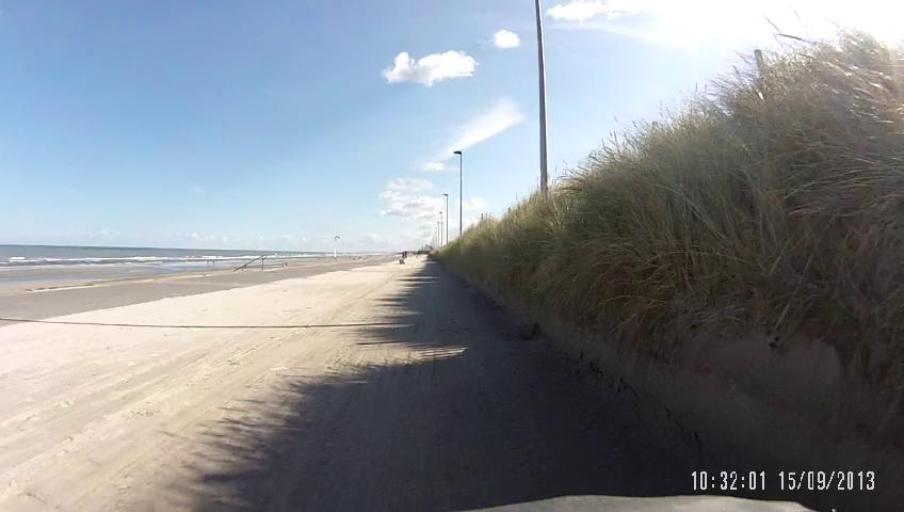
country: FR
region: Nord-Pas-de-Calais
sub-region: Departement du Nord
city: Coudekerque-Branche
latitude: 51.0548
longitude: 2.4187
